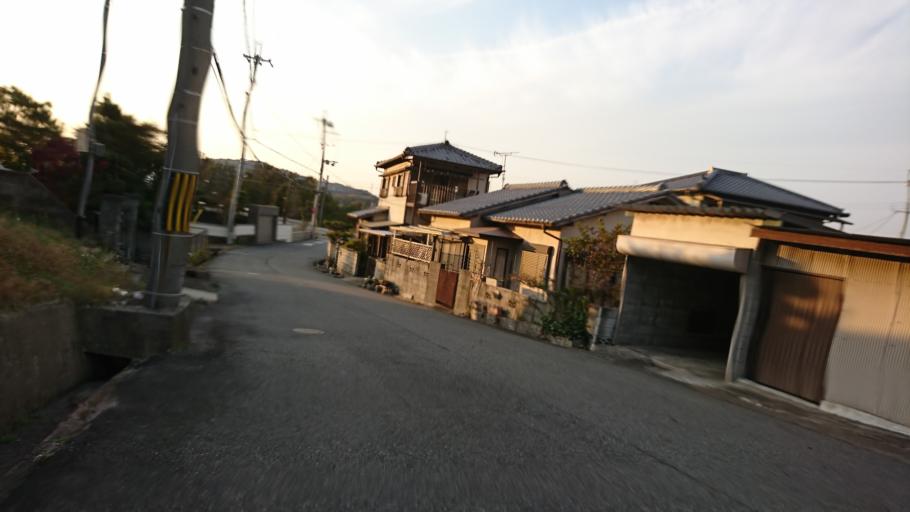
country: JP
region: Hyogo
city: Kakogawacho-honmachi
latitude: 34.7845
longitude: 134.8662
